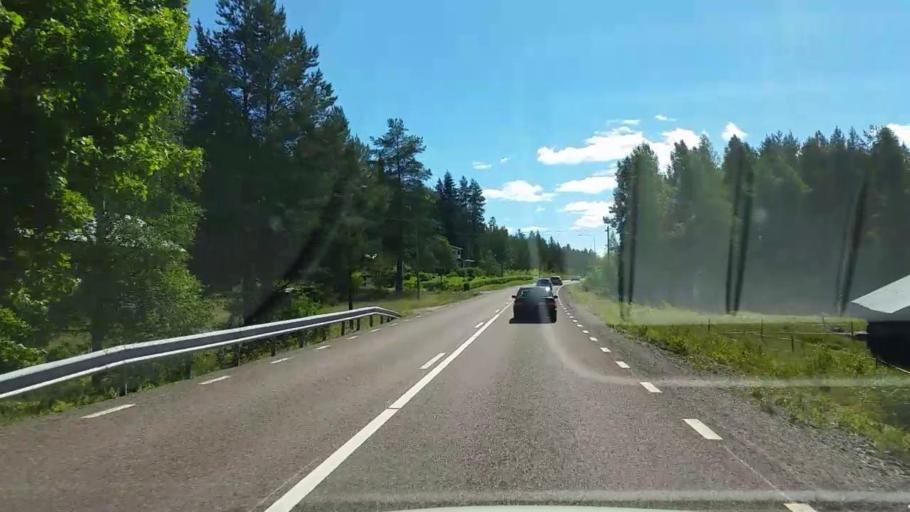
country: SE
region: Gaevleborg
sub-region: Ovanakers Kommun
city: Edsbyn
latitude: 61.2698
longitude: 15.8927
